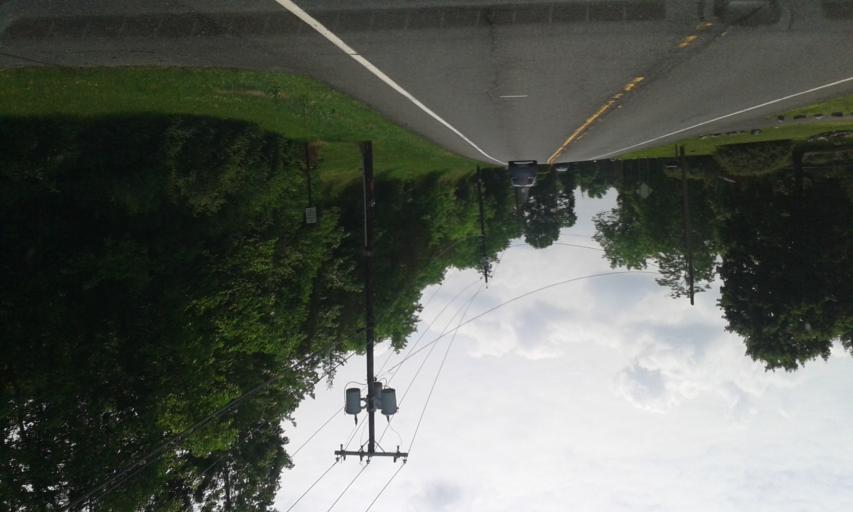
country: US
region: New Jersey
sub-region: Hunterdon County
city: Whitehouse Station
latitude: 40.6367
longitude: -74.7644
